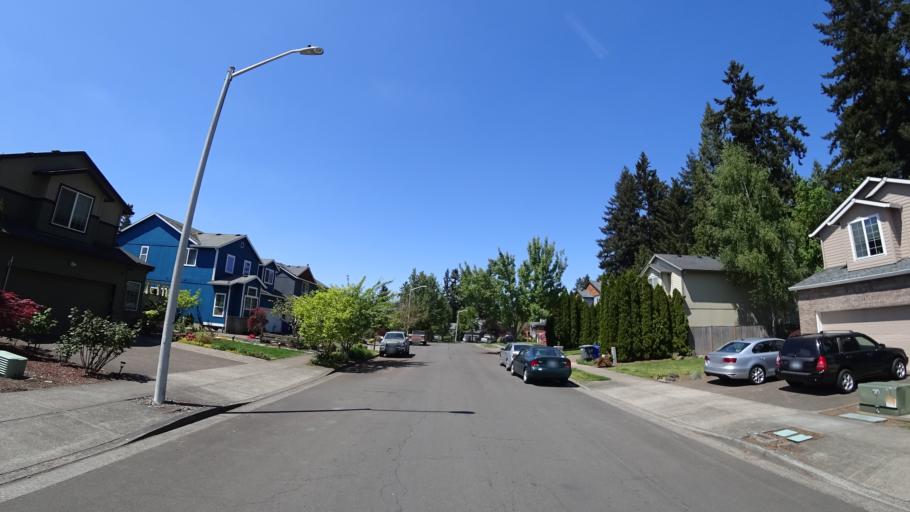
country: US
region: Oregon
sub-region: Washington County
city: Rockcreek
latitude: 45.5194
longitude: -122.9039
